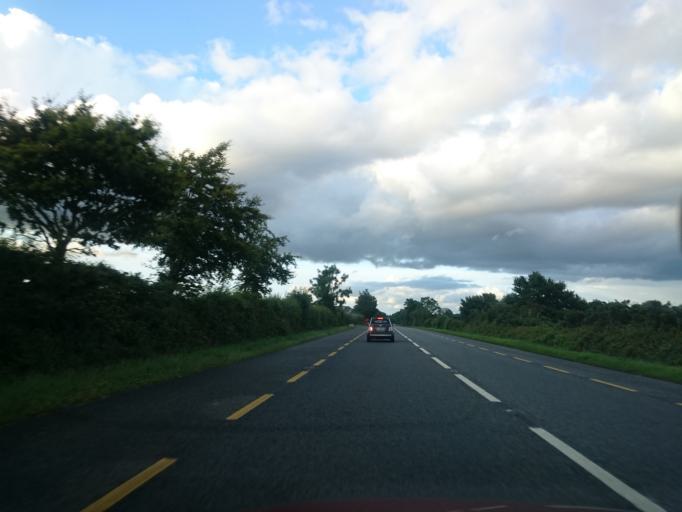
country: IE
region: Leinster
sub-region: Loch Garman
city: Enniscorthy
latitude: 52.5502
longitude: -6.5441
